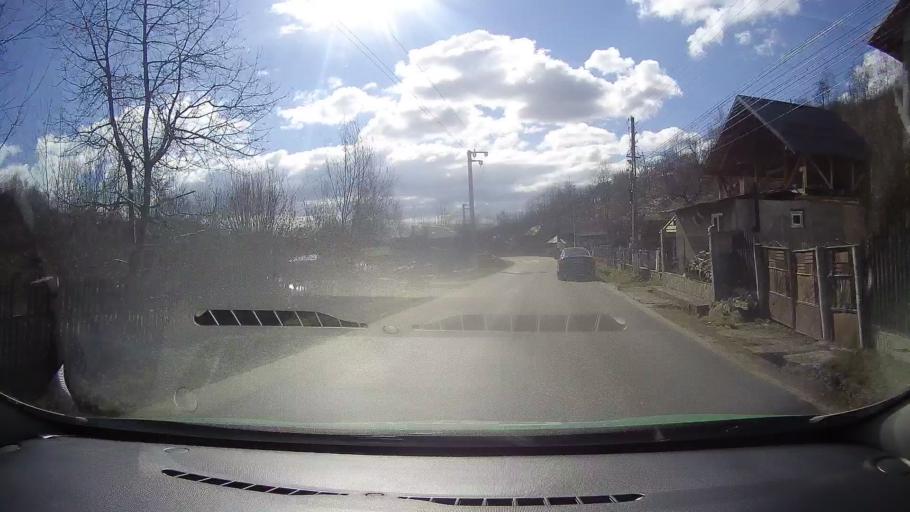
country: RO
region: Dambovita
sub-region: Comuna Runcu
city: Badeni
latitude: 45.1656
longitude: 25.3952
